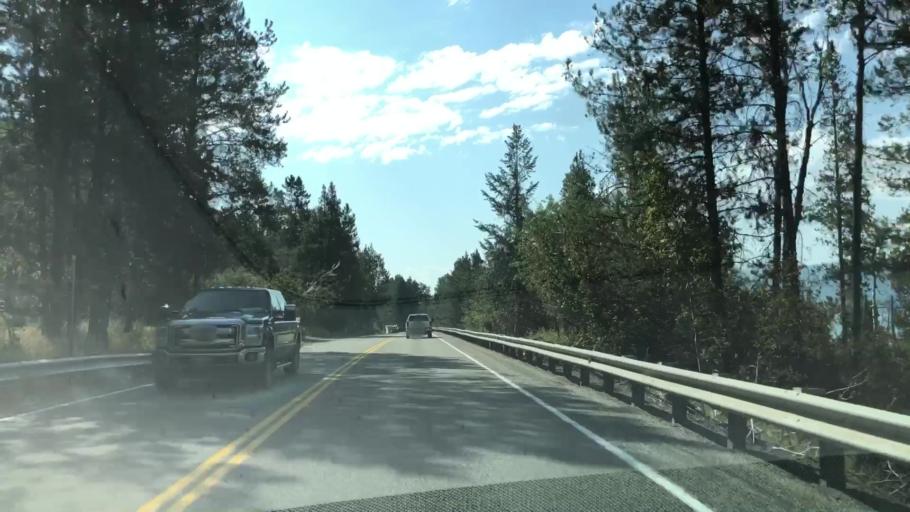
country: US
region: Idaho
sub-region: Teton County
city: Victor
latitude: 43.3058
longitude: -111.1352
